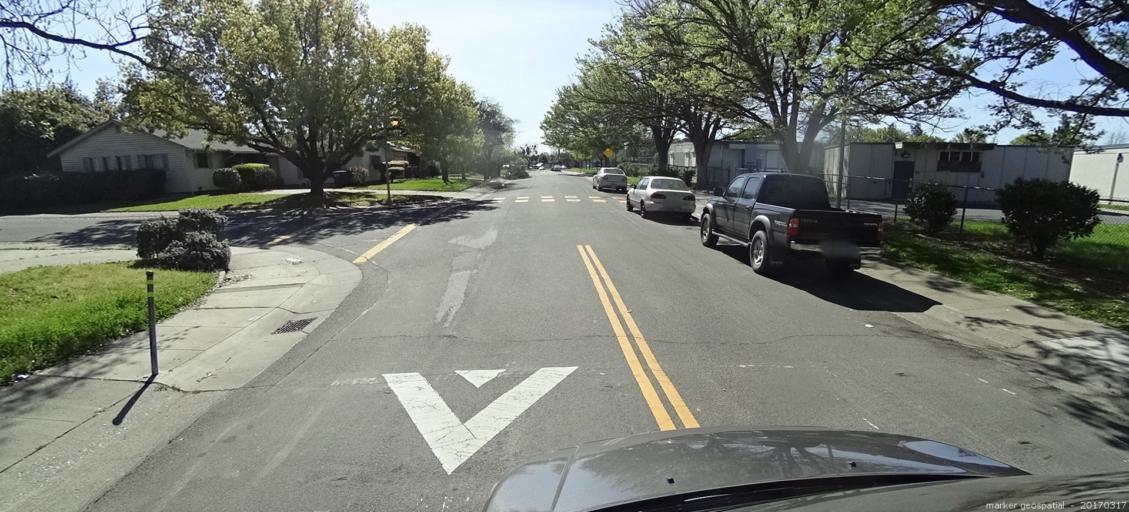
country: US
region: California
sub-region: Sacramento County
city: Parkway
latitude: 38.4924
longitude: -121.4960
